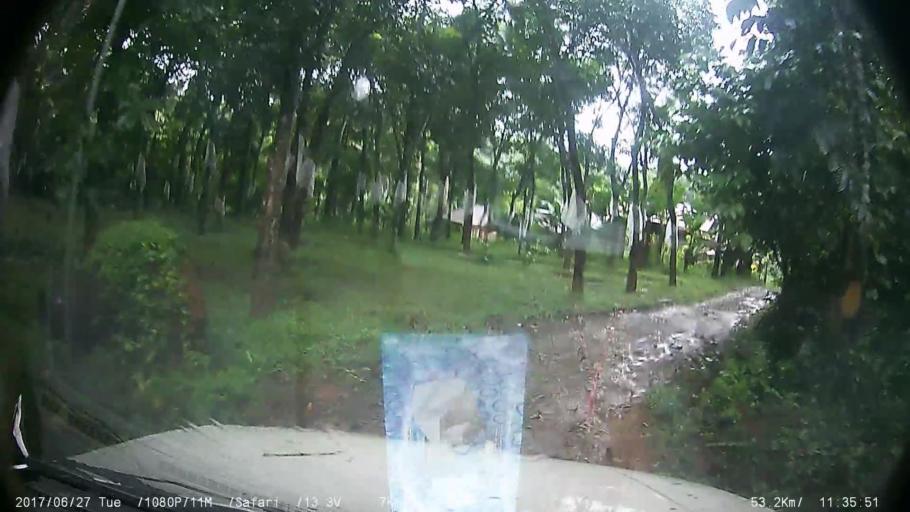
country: IN
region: Kerala
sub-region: Kottayam
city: Palackattumala
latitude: 9.7634
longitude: 76.5774
